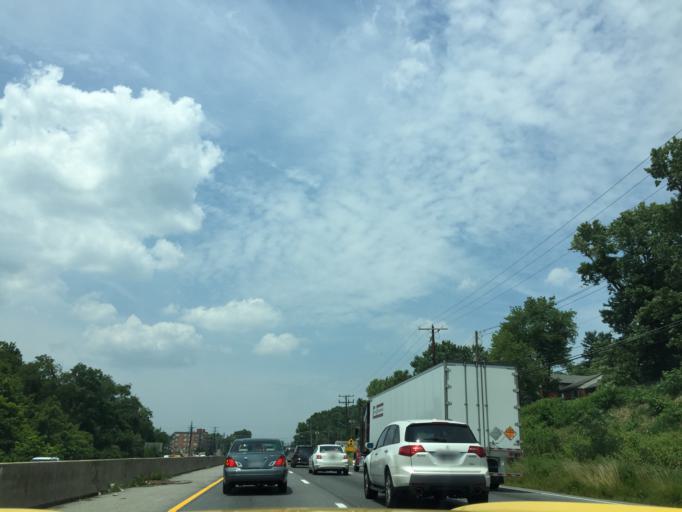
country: US
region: Maryland
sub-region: Prince George's County
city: Oxon Hill
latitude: 38.7773
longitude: -76.9967
